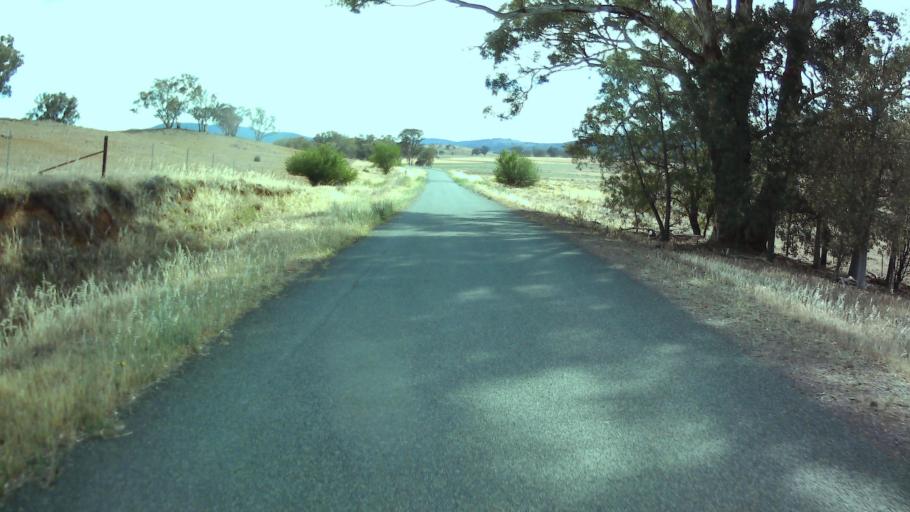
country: AU
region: New South Wales
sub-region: Weddin
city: Grenfell
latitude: -33.8256
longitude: 148.2867
